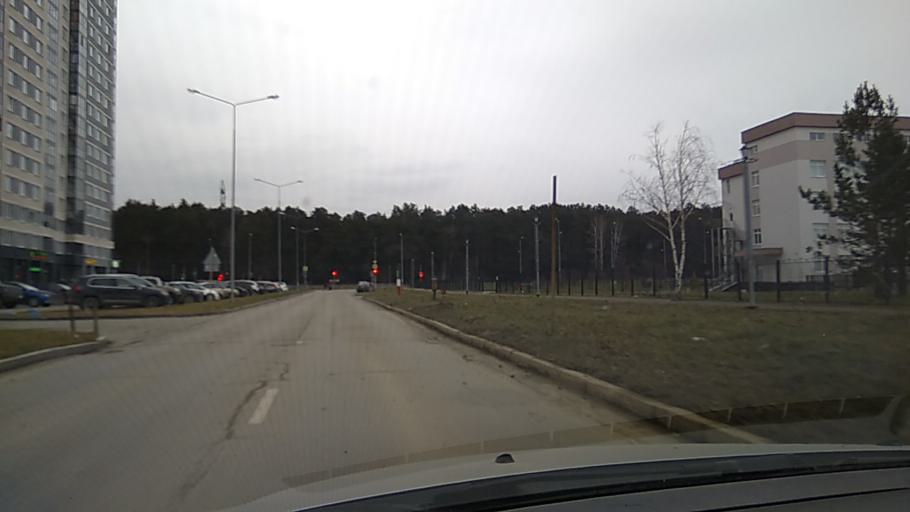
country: RU
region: Sverdlovsk
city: Sovkhoznyy
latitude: 56.7815
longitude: 60.5532
